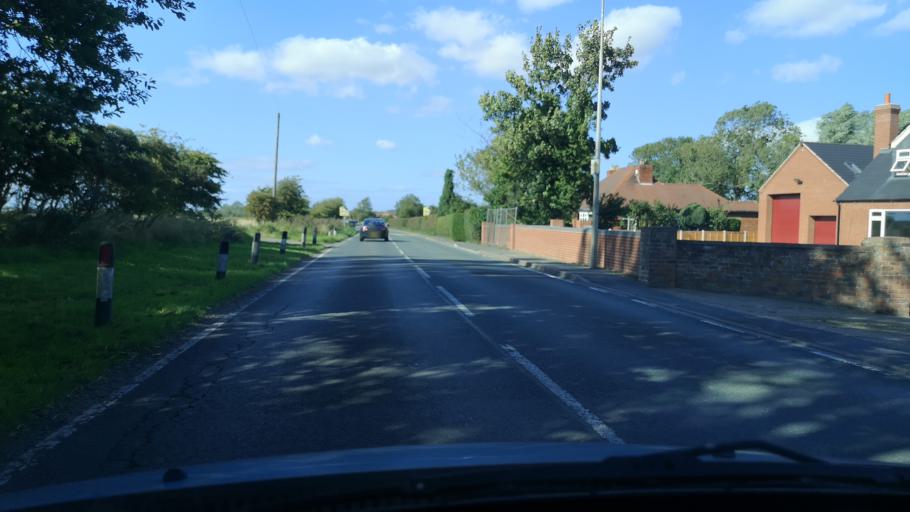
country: GB
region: England
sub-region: North Lincolnshire
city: Belton
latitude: 53.5574
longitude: -0.8166
